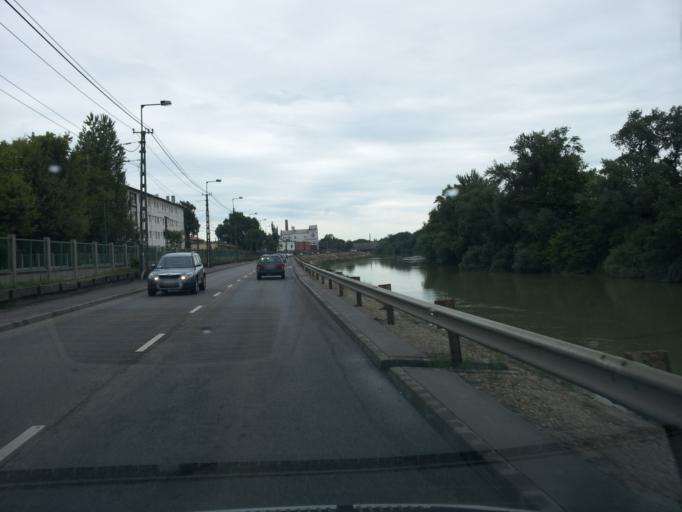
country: HU
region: Budapest
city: Budapest III. keruelet
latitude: 47.5428
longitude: 19.0470
